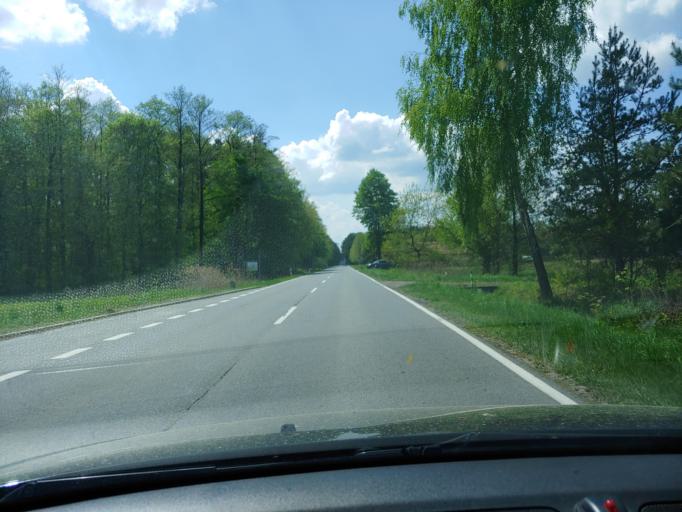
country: PL
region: Lesser Poland Voivodeship
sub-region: Powiat dabrowski
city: Radgoszcz
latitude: 50.1413
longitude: 21.1744
